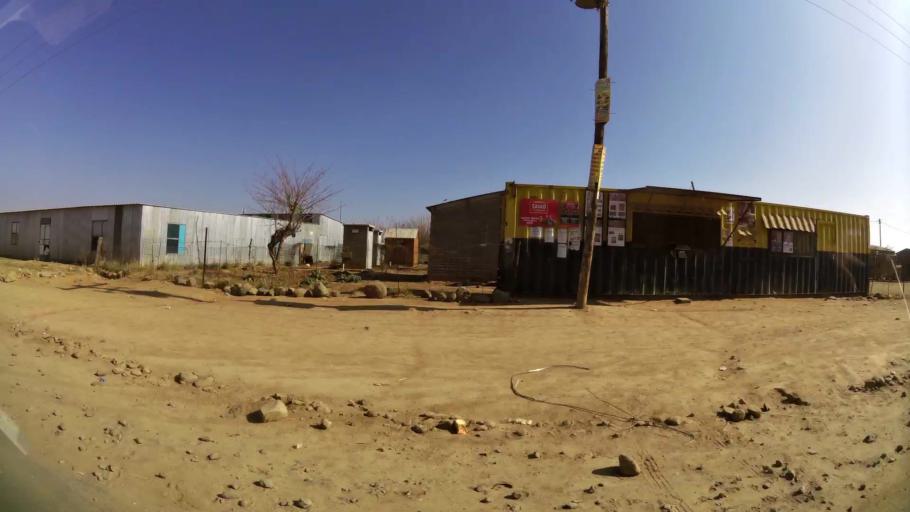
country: ZA
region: Orange Free State
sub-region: Mangaung Metropolitan Municipality
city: Bloemfontein
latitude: -29.1918
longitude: 26.2827
